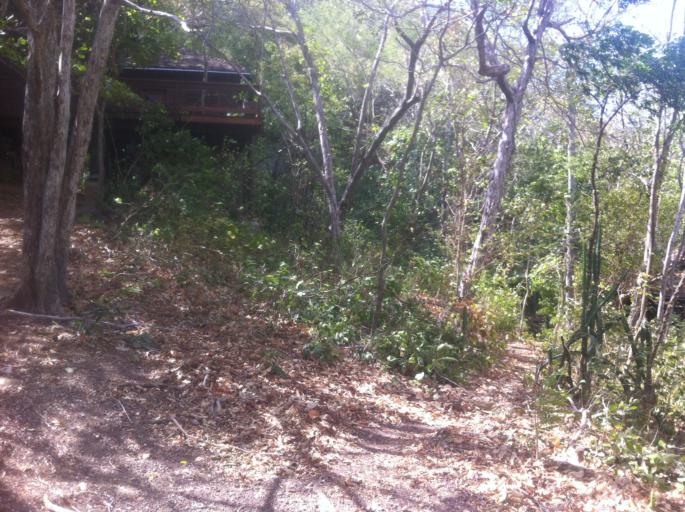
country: NI
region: Rivas
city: Tola
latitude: 11.3820
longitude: -86.0288
